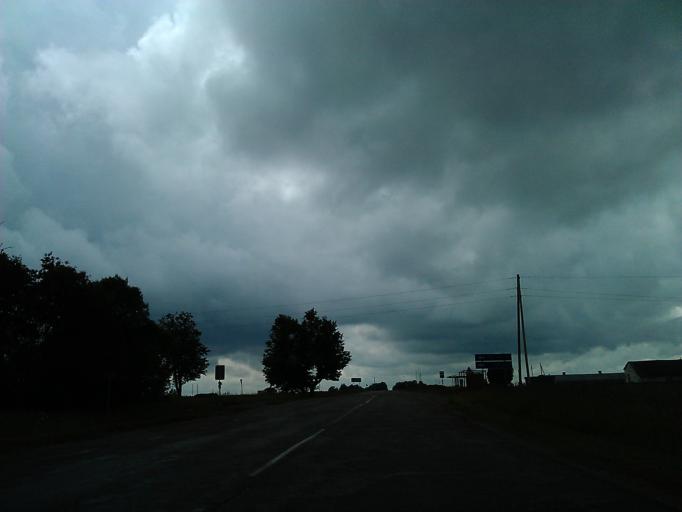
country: LV
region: Aizpute
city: Aizpute
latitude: 56.8406
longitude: 21.7673
